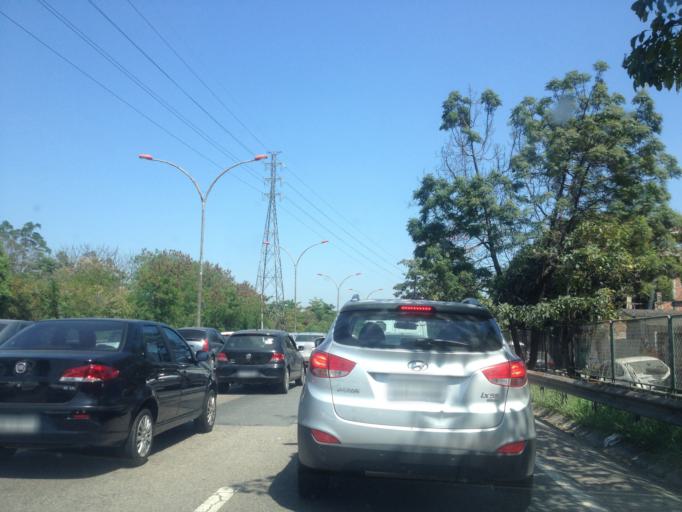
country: BR
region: Rio de Janeiro
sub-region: Duque De Caxias
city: Duque de Caxias
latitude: -22.8004
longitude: -43.3208
